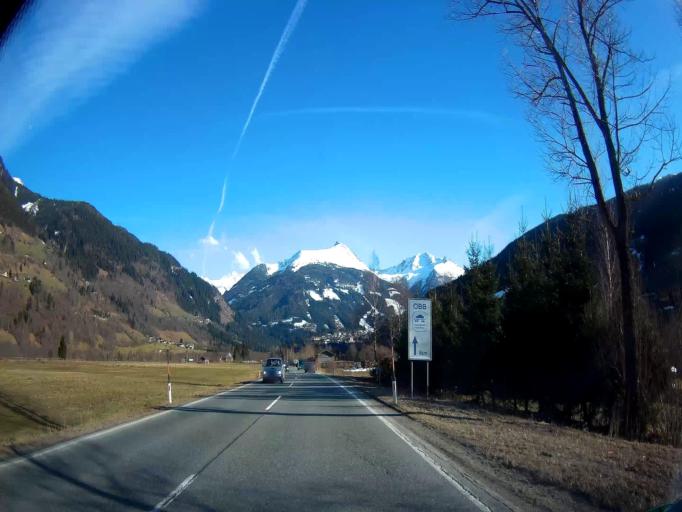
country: AT
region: Salzburg
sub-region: Politischer Bezirk Sankt Johann im Pongau
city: Bad Hofgastein
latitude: 47.1469
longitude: 13.1159
